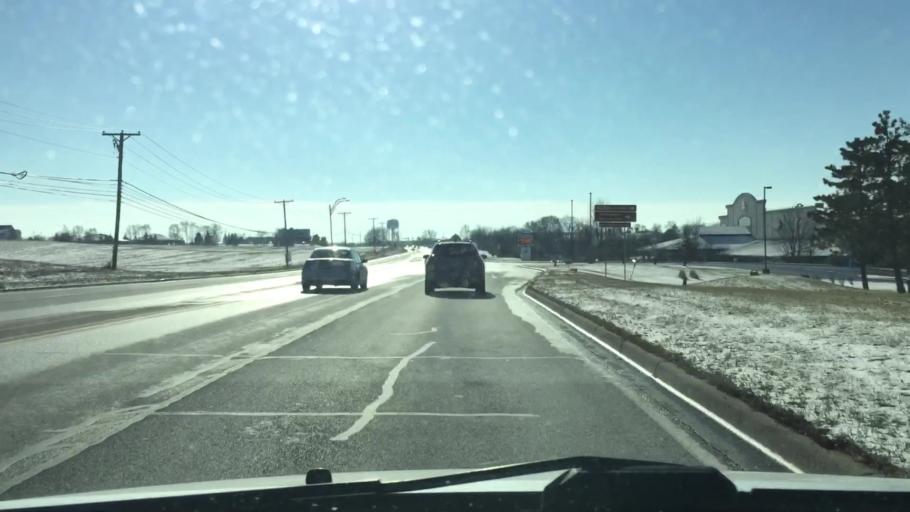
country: US
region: Illinois
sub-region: Kane County
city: Geneva
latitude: 41.8747
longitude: -88.2785
